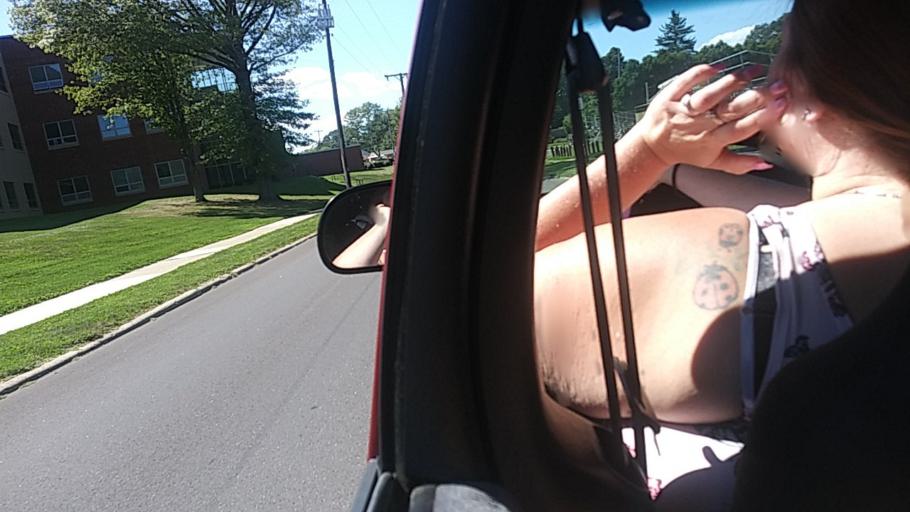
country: US
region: Ohio
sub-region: Summit County
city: Fairlawn
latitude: 41.1195
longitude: -81.5634
